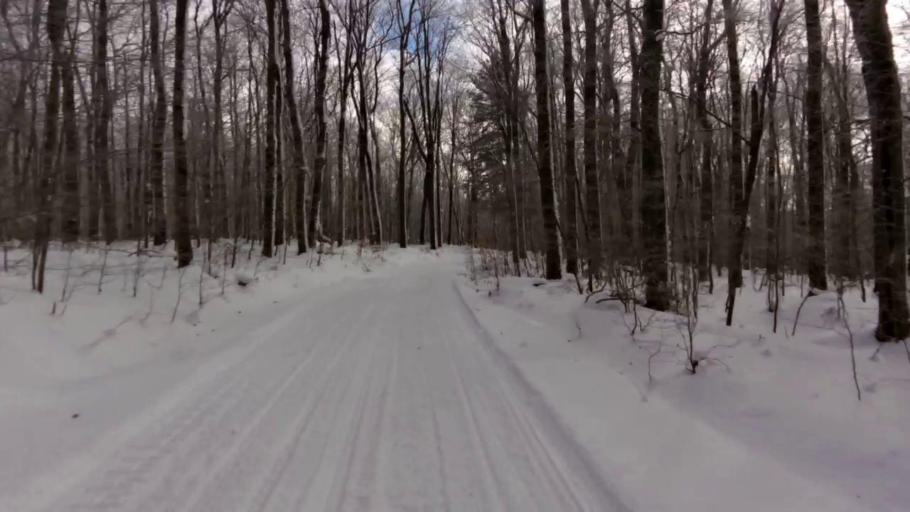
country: US
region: New York
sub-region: Cattaraugus County
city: Salamanca
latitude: 42.0554
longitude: -78.7683
